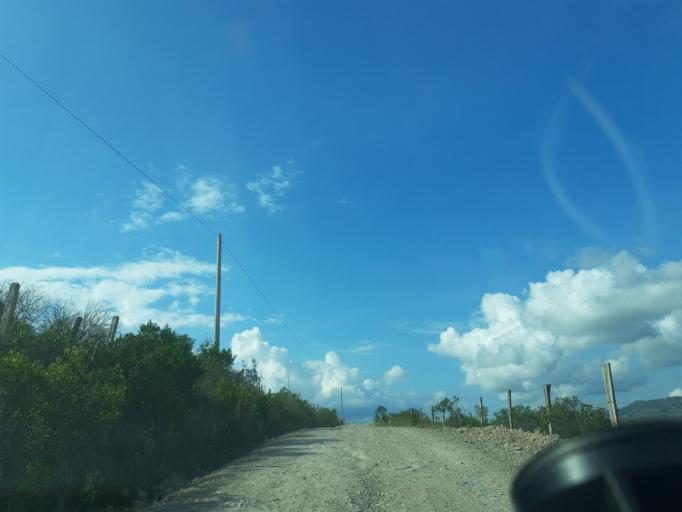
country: CO
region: Boyaca
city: Villa de Leiva
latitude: 5.6631
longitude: -73.5531
